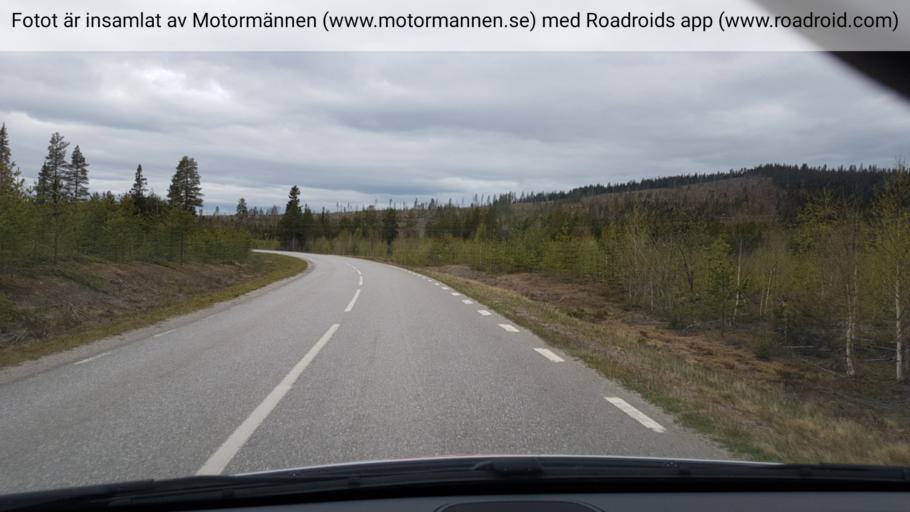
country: SE
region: Vaesterbotten
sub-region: Sorsele Kommun
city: Sorsele
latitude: 65.5423
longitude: 17.4036
